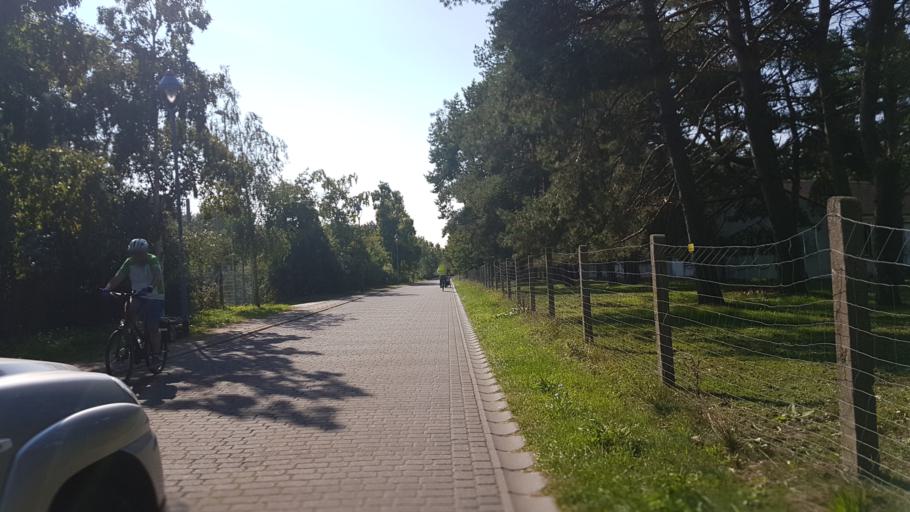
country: DE
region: Mecklenburg-Vorpommern
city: Ostseebad Gohren
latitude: 54.3348
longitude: 13.7332
